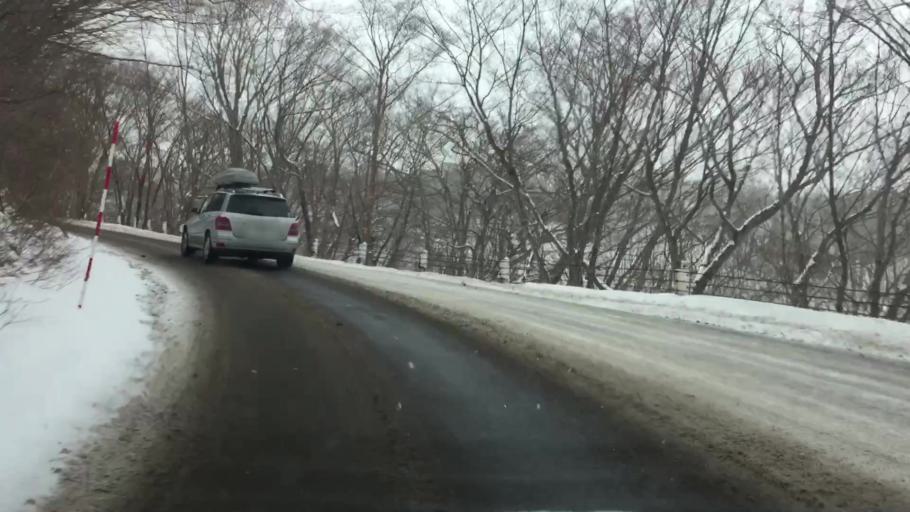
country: JP
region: Tochigi
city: Yaita
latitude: 36.9697
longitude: 139.7895
